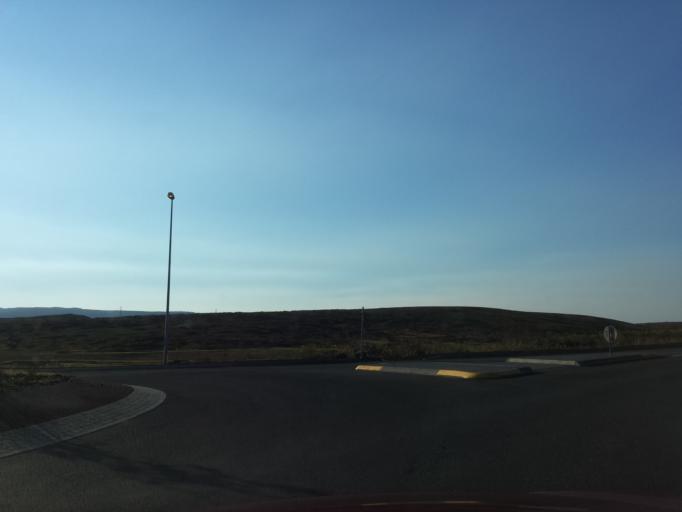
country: IS
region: Capital Region
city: Reykjavik
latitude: 64.0829
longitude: -21.8349
